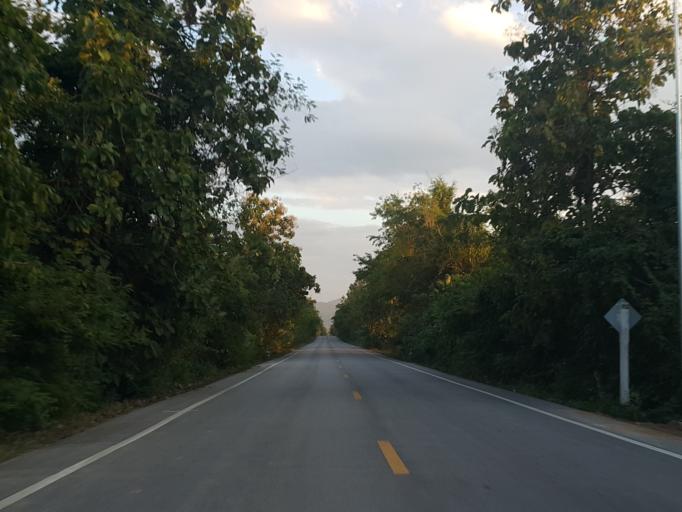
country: TH
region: Lampang
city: Mae Mo
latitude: 18.4471
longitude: 99.6357
